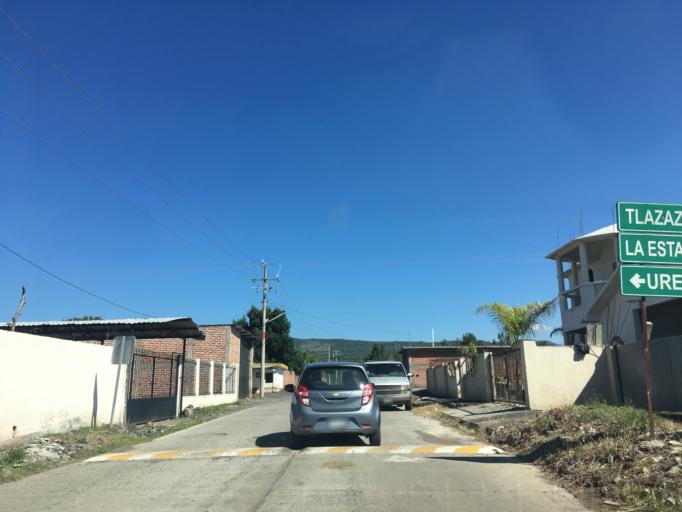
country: MX
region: Mexico
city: Tlazazalca
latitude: 19.9755
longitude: -102.1198
